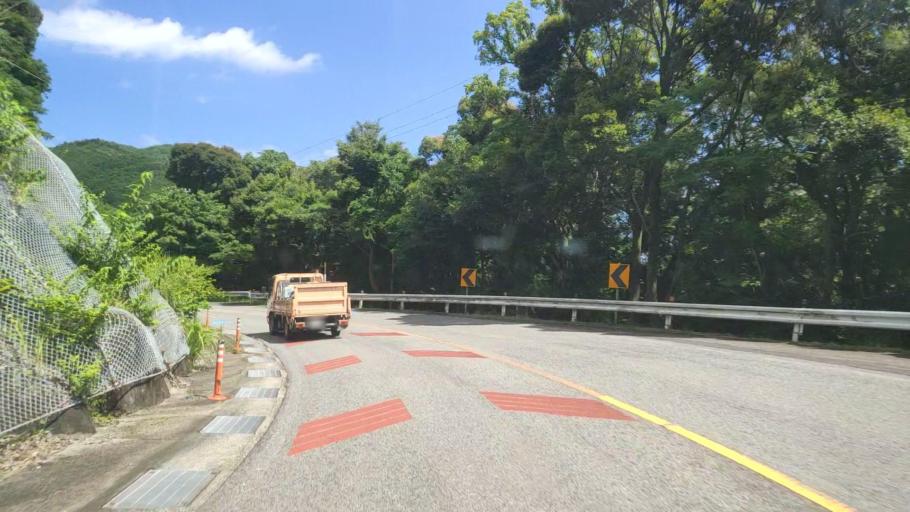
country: JP
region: Mie
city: Owase
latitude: 33.9182
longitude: 136.1082
